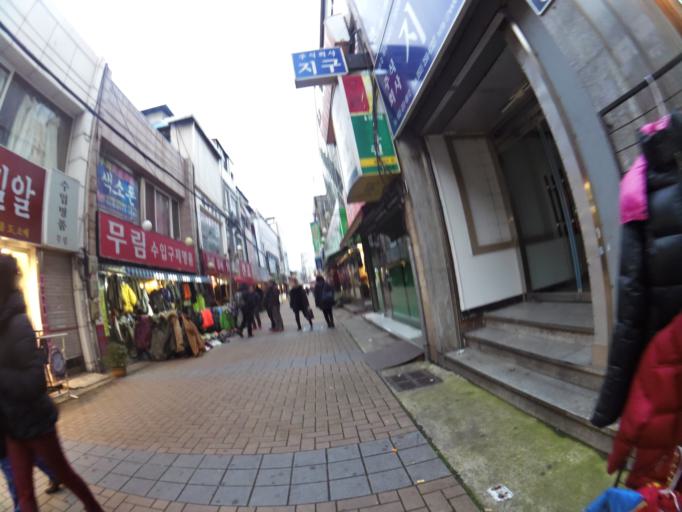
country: KR
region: Daegu
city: Daegu
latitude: 35.8732
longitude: 128.5949
